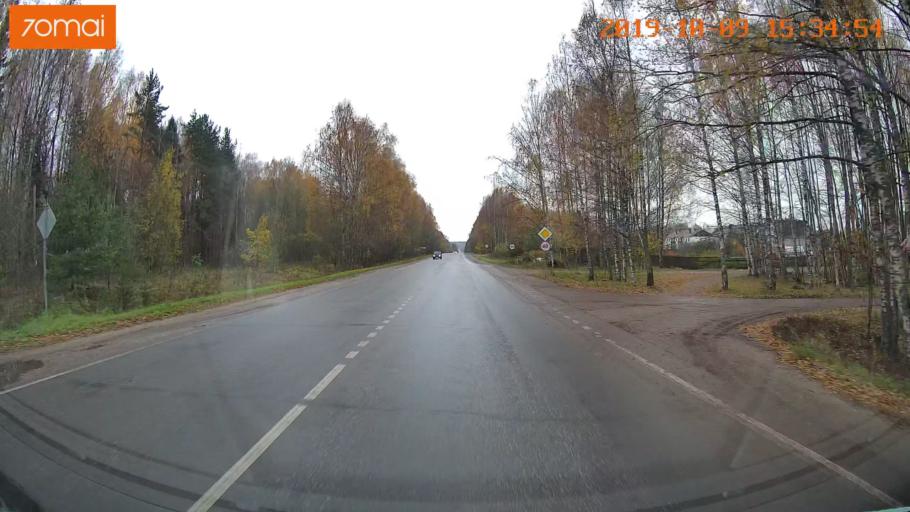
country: RU
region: Kostroma
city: Oktyabr'skiy
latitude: 57.9371
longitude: 41.2374
